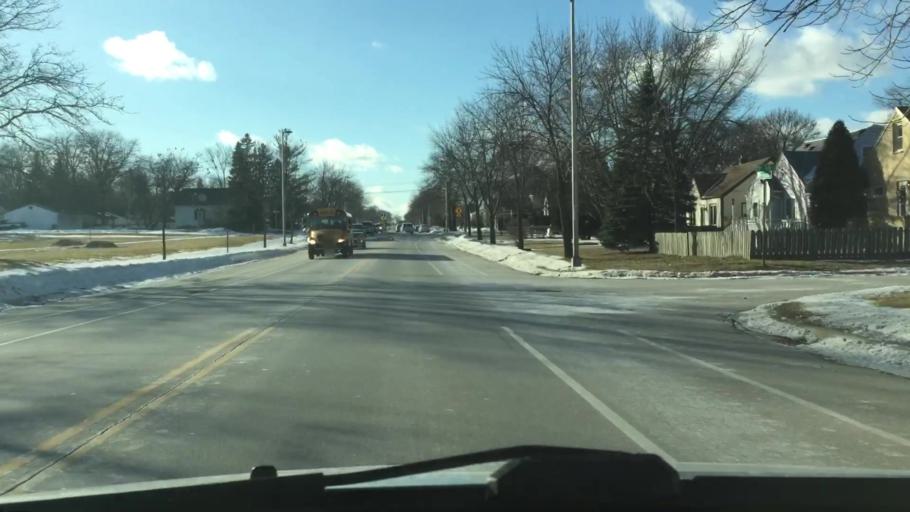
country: US
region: Wisconsin
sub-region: Milwaukee County
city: West Milwaukee
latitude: 42.9740
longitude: -87.9631
